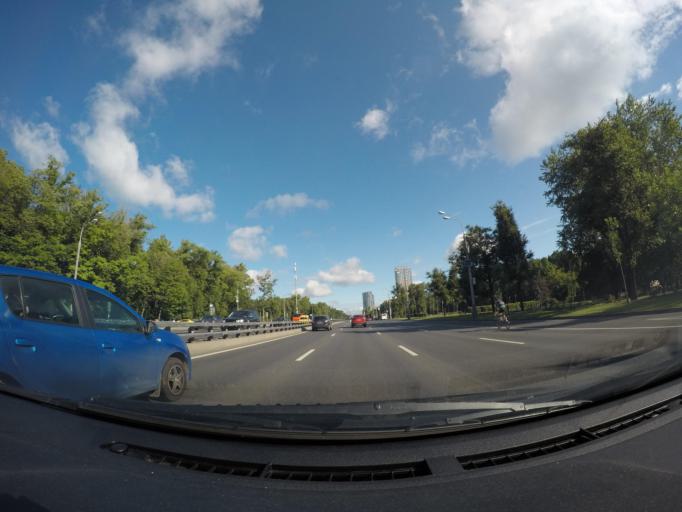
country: RU
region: Moskovskaya
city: Levoberezhnyy
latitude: 55.8505
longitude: 37.4736
